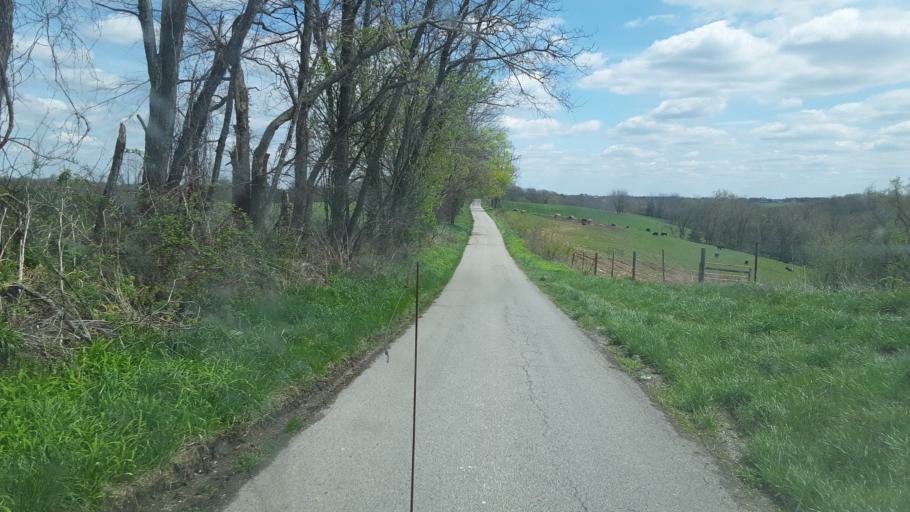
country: US
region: Kentucky
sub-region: Owen County
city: Owenton
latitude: 38.6742
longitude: -84.8110
